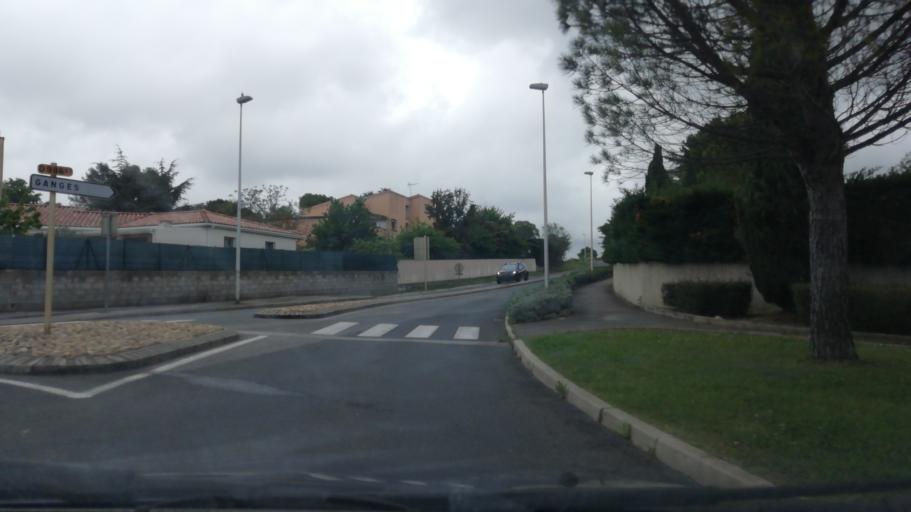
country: FR
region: Languedoc-Roussillon
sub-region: Departement de l'Herault
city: Saint-Gely-du-Fesc
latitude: 43.7010
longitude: 3.8036
